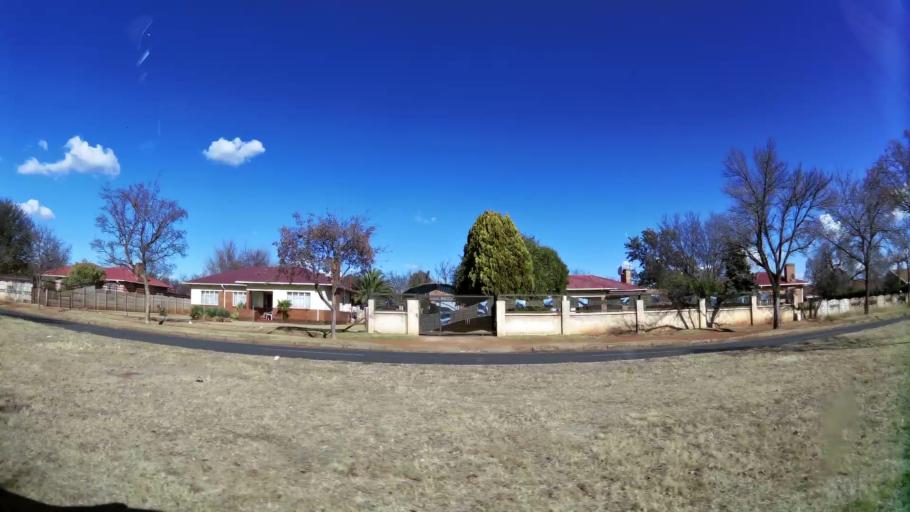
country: ZA
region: Gauteng
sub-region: West Rand District Municipality
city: Carletonville
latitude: -26.3577
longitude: 27.3882
